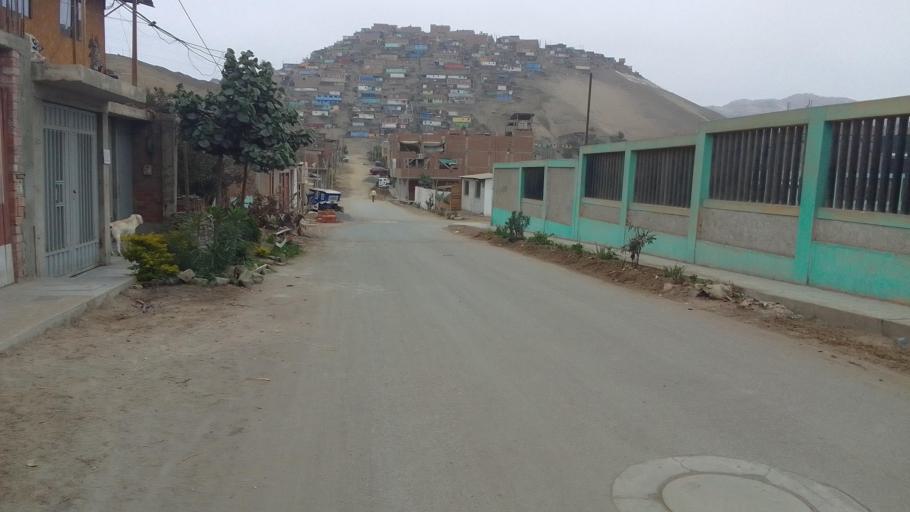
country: PE
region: Lima
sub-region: Lima
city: Santa Rosa
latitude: -11.8172
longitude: -77.1243
